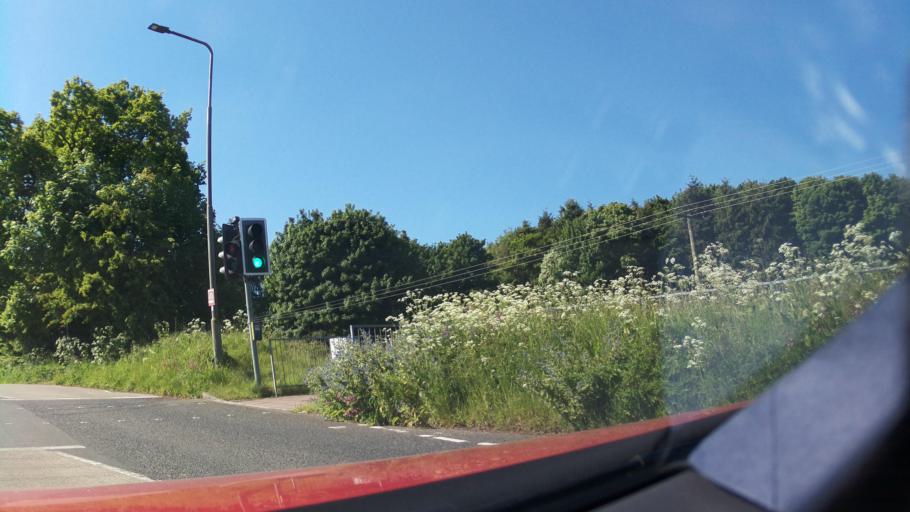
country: GB
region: Scotland
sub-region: Fife
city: Newport-On-Tay
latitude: 56.4326
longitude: -2.9369
